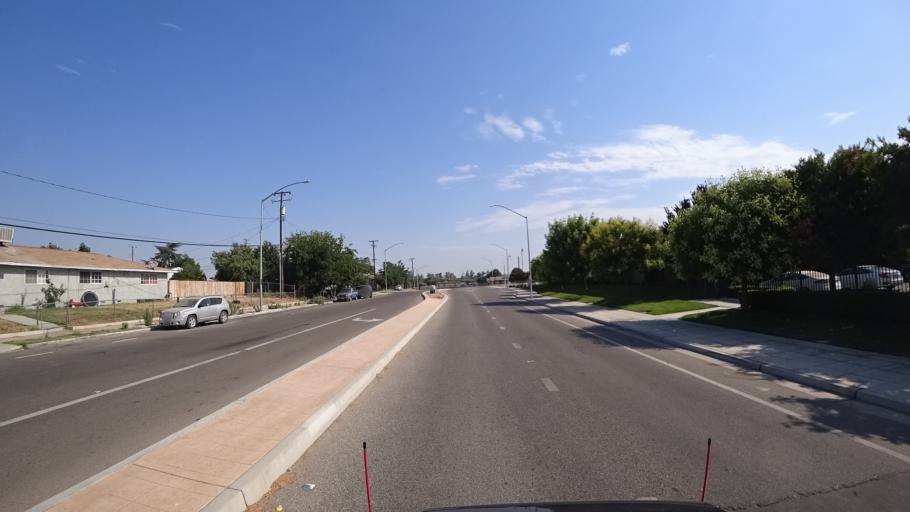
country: US
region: California
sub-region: Fresno County
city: West Park
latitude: 36.7197
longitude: -119.8110
